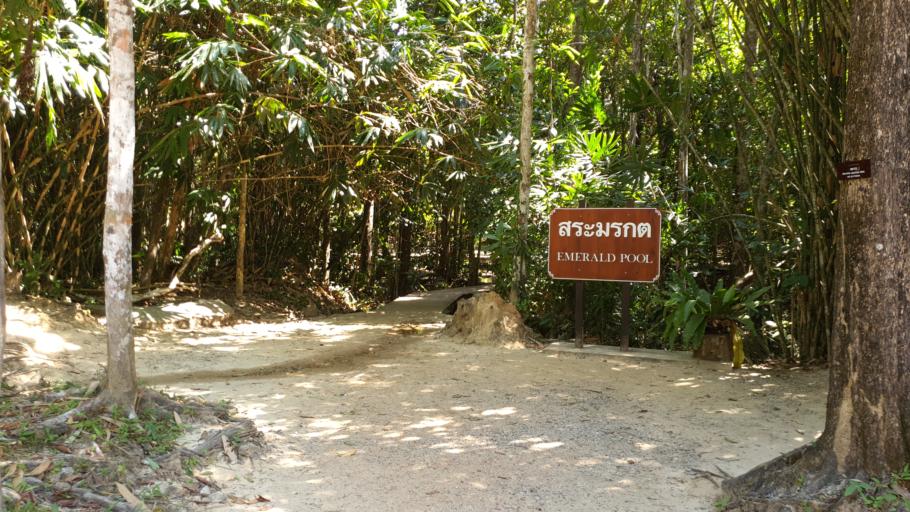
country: TH
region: Krabi
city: Khlong Thom
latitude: 7.9255
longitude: 99.2675
